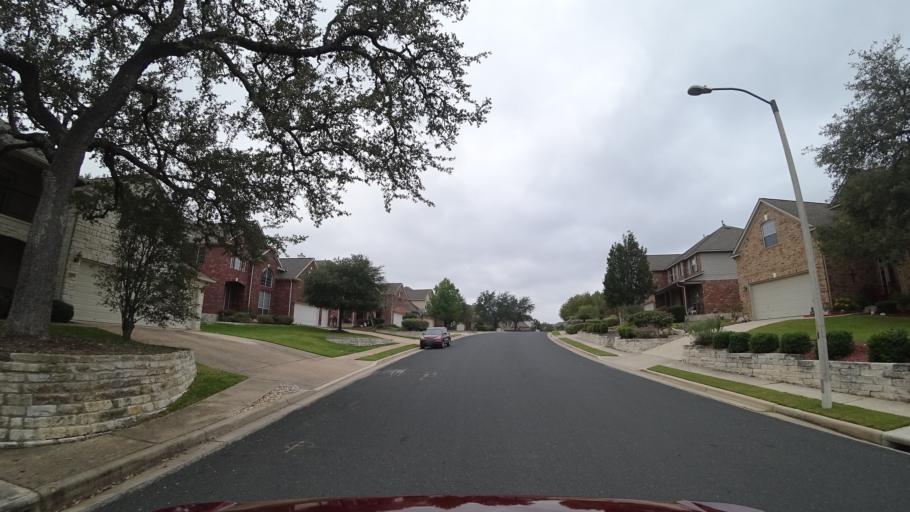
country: US
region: Texas
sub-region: Williamson County
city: Anderson Mill
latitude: 30.4332
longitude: -97.8184
